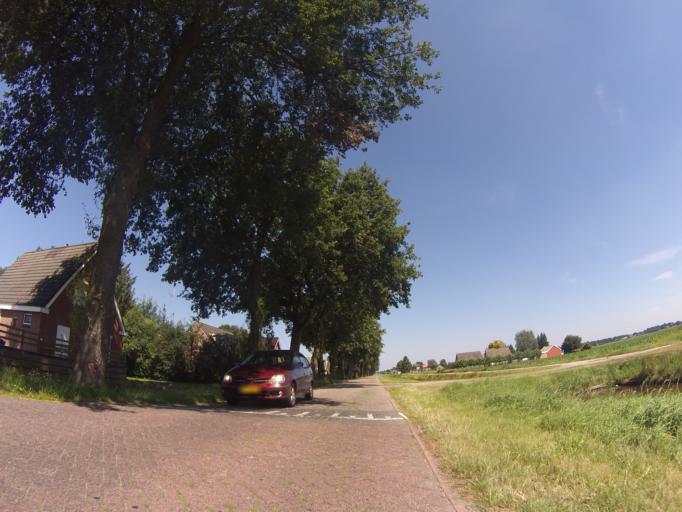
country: NL
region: Drenthe
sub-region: Gemeente Emmen
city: Klazienaveen
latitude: 52.7133
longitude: 7.0463
